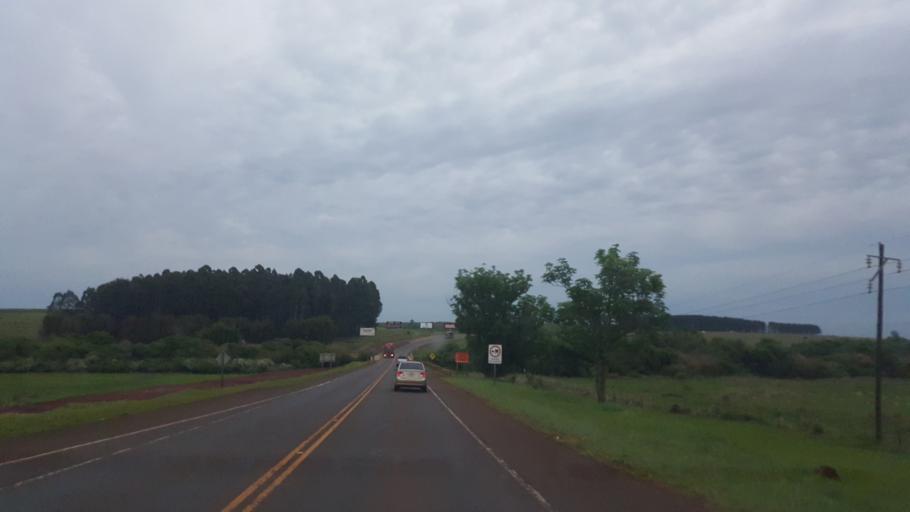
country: AR
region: Misiones
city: Garupa
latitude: -27.5825
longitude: -55.8440
